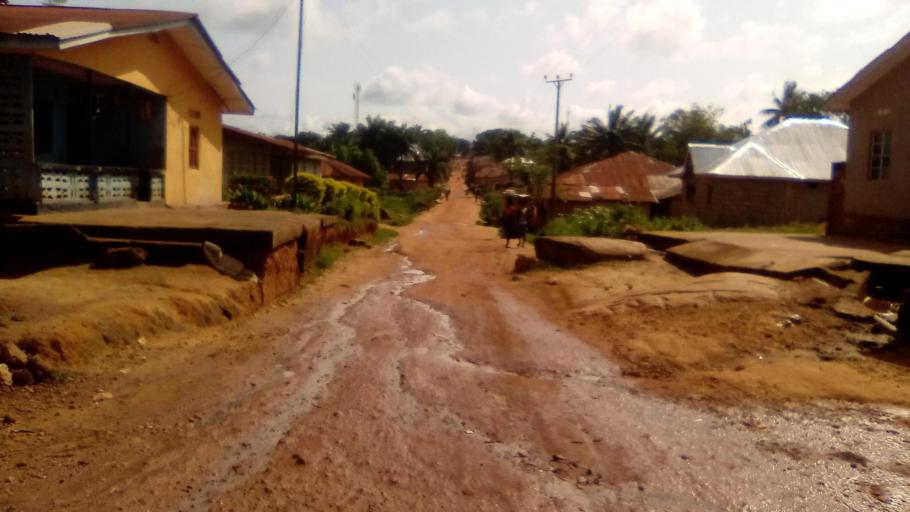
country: SL
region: Southern Province
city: Bo
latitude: 7.9748
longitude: -11.7298
